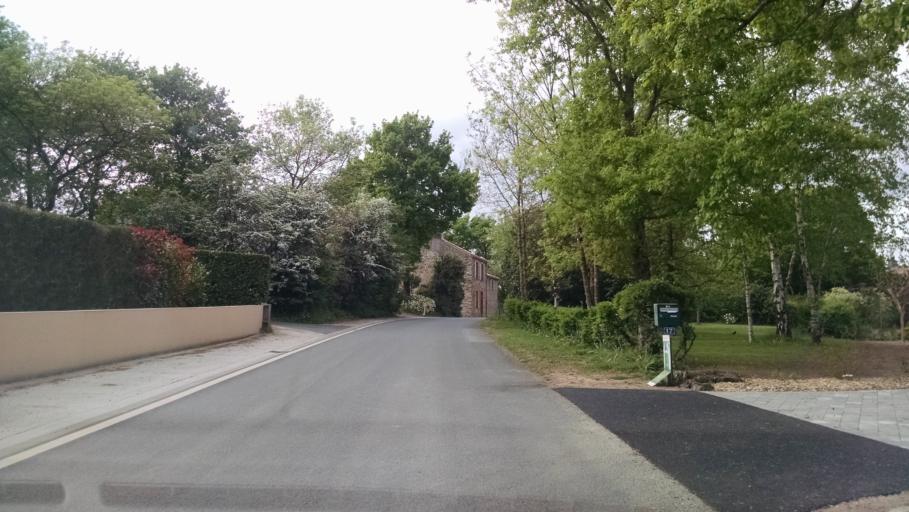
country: FR
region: Pays de la Loire
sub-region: Departement de la Vendee
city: Bouffere
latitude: 46.9778
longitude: -1.3321
